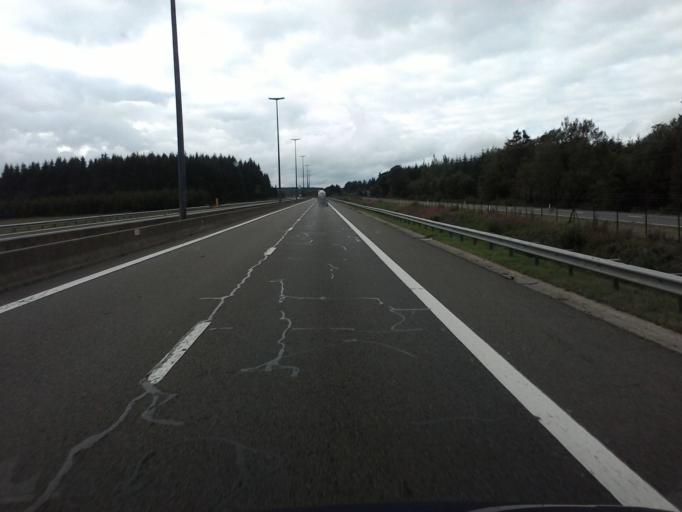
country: BE
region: Wallonia
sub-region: Province de Liege
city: Lierneux
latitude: 50.2363
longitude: 5.7588
